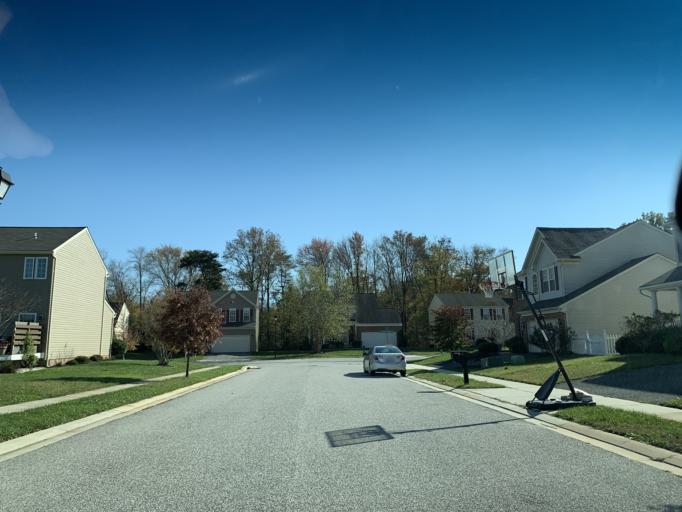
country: US
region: Maryland
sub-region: Baltimore County
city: White Marsh
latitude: 39.4054
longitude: -76.4120
